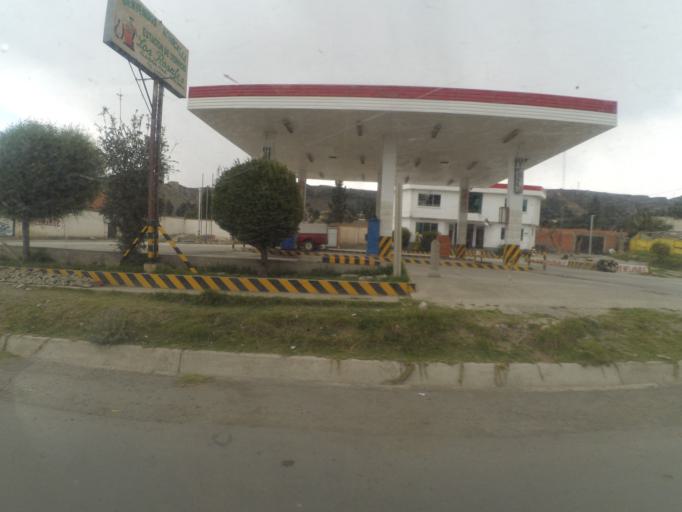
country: BO
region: La Paz
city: La Paz
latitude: -16.5725
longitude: -68.1725
